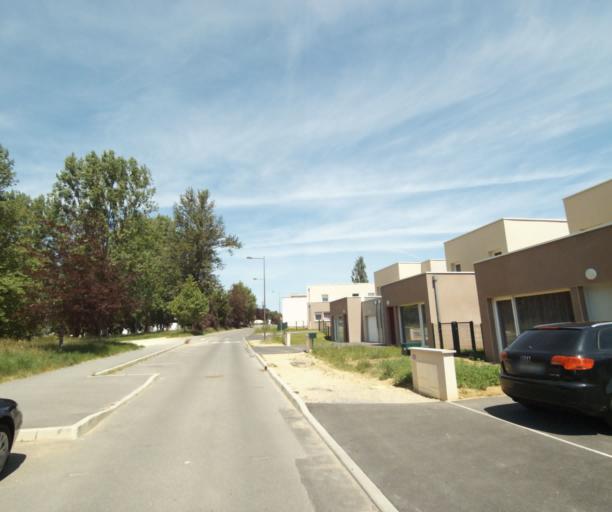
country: FR
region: Champagne-Ardenne
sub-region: Departement des Ardennes
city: Charleville-Mezieres
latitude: 49.7496
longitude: 4.7177
